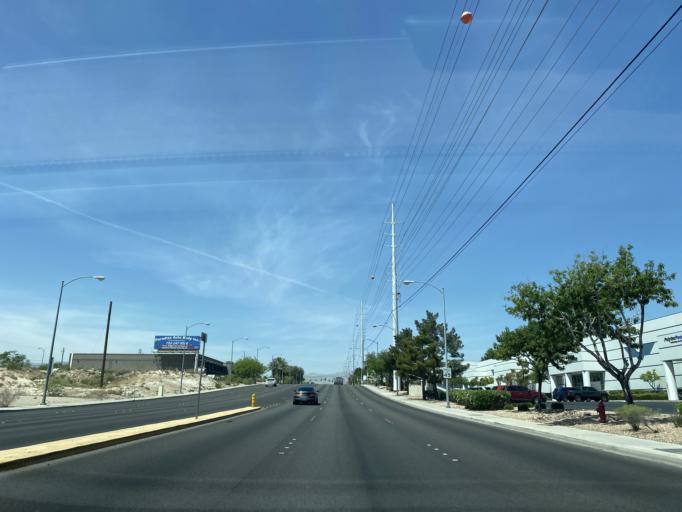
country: US
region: Nevada
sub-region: Clark County
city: Spring Valley
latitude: 36.0864
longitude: -115.1996
